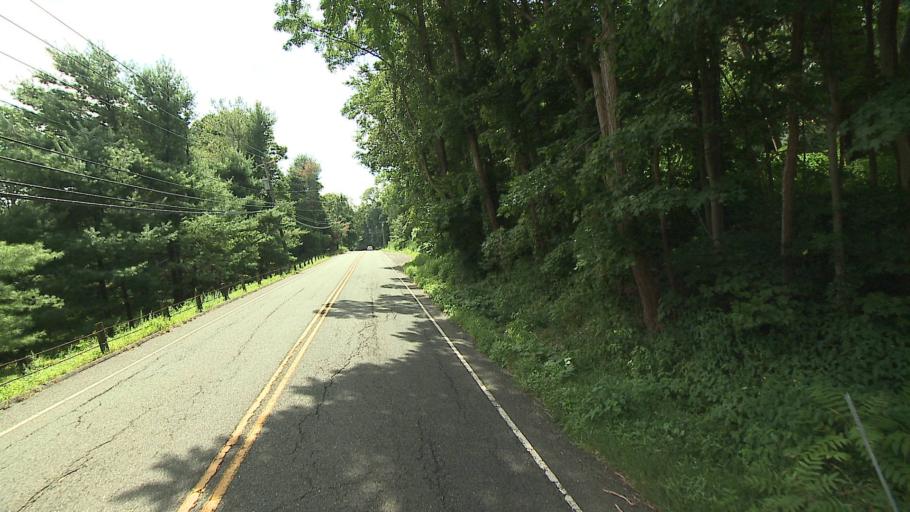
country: US
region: Connecticut
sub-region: Fairfield County
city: Sherman
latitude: 41.5577
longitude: -73.4898
